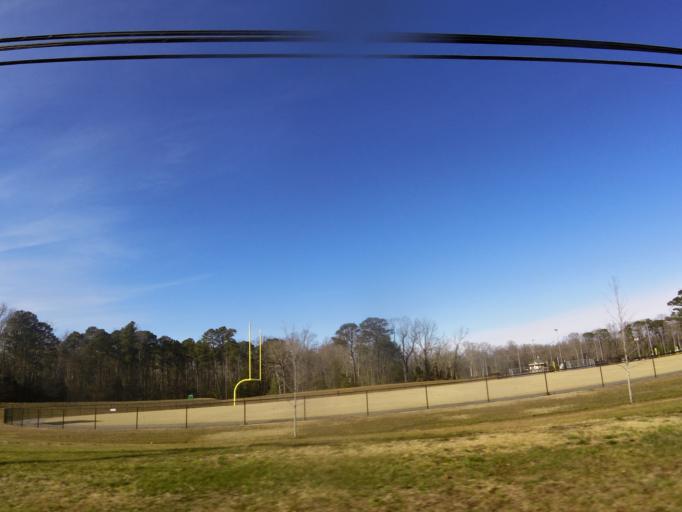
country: US
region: Virginia
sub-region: Isle of Wight County
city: Smithfield
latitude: 36.9723
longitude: -76.6530
